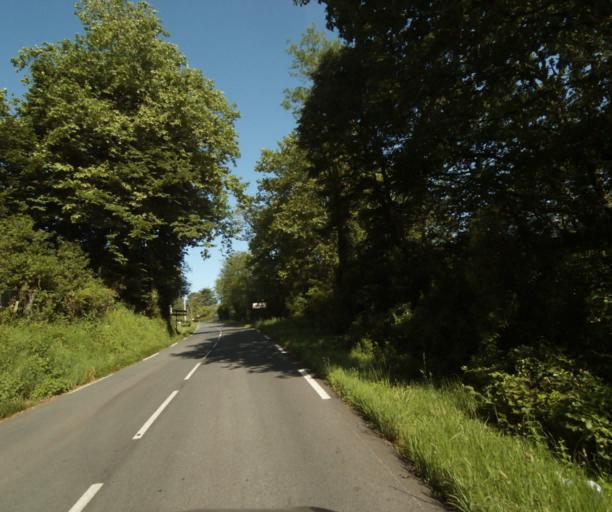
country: FR
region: Aquitaine
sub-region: Departement des Pyrenees-Atlantiques
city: Mouguerre
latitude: 43.4673
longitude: -1.4359
